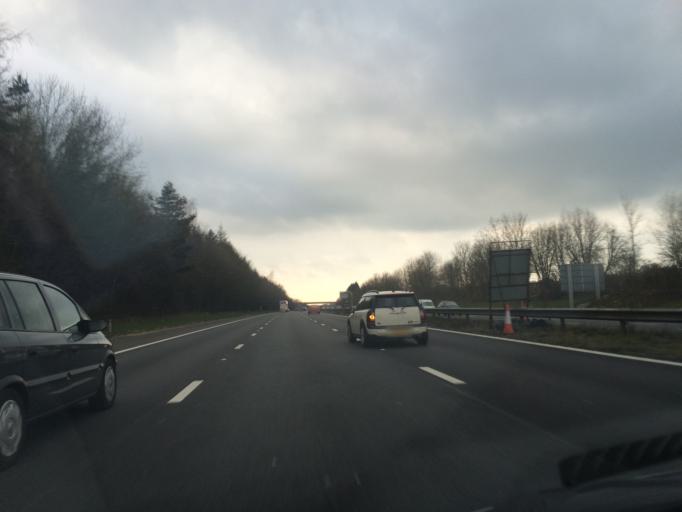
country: GB
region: England
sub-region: West Berkshire
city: Wickham
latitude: 51.4490
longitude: -1.4655
